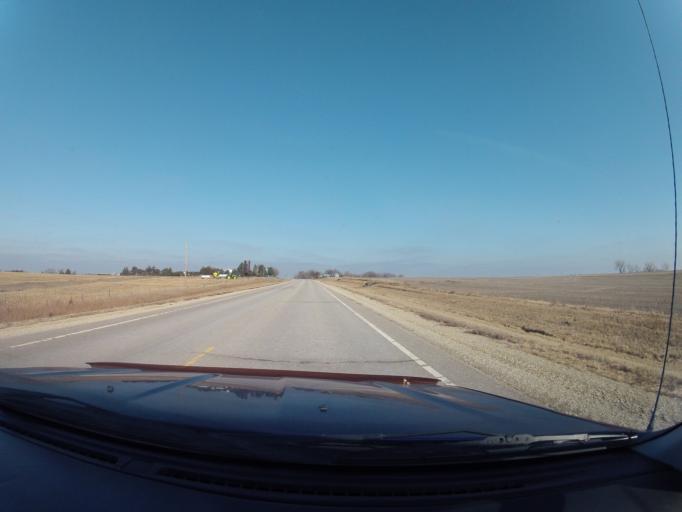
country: US
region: Kansas
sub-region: Marshall County
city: Blue Rapids
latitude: 39.5913
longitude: -96.7501
